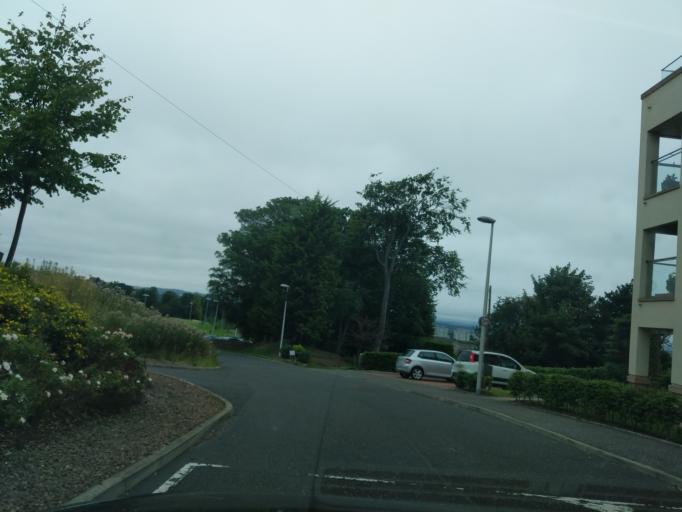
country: GB
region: Scotland
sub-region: Edinburgh
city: Currie
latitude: 55.9065
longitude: -3.2869
